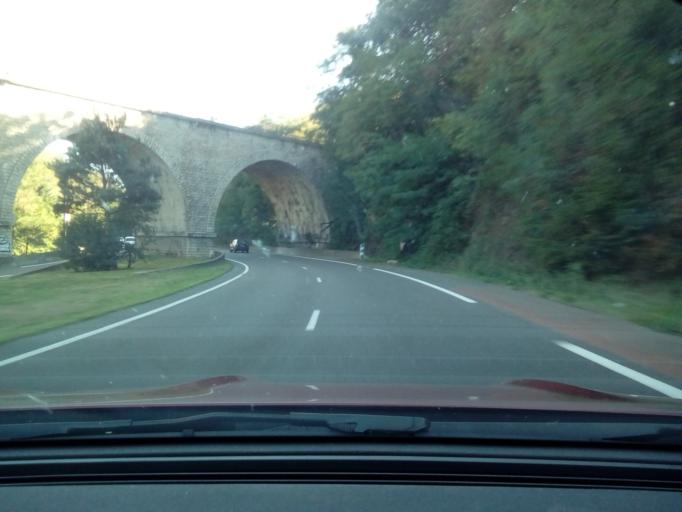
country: FR
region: Rhone-Alpes
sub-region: Departement du Rhone
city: Lozanne
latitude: 45.8523
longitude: 4.7172
